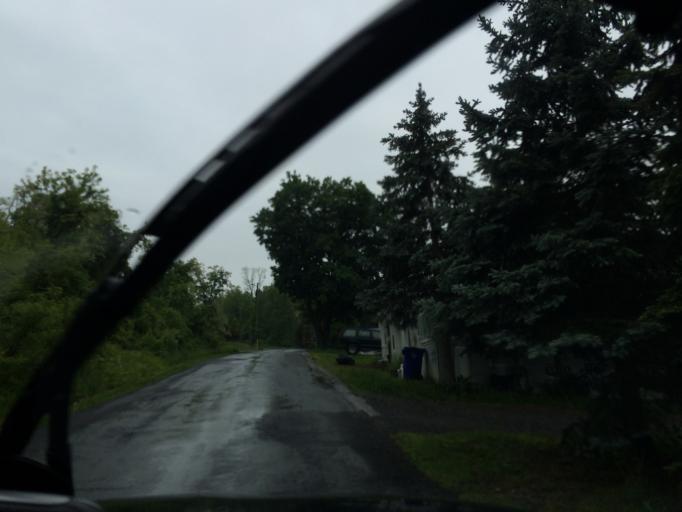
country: US
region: Maryland
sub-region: Washington County
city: Highfield-Cascade
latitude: 39.6995
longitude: -77.4760
